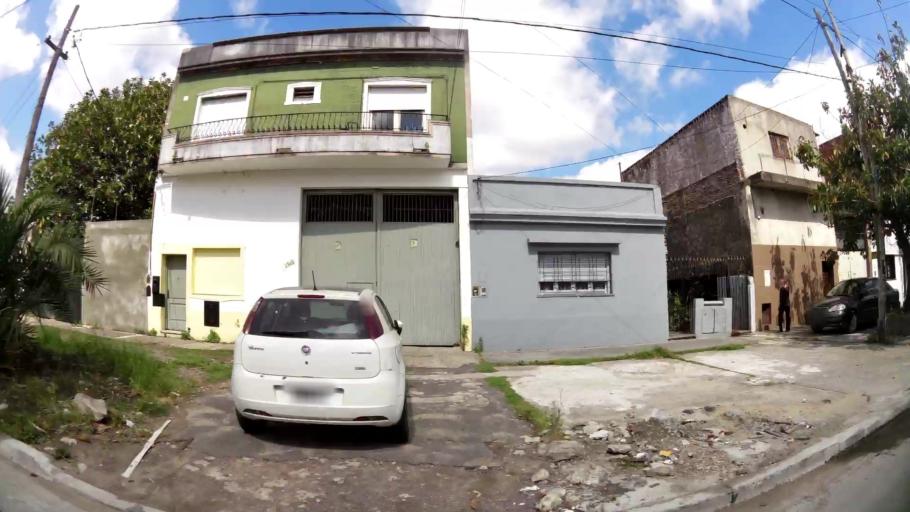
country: AR
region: Buenos Aires
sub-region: Partido de Lanus
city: Lanus
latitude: -34.6839
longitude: -58.4193
